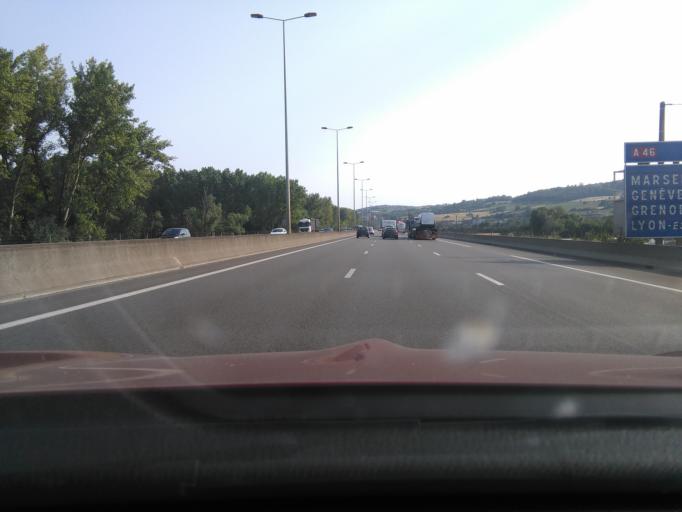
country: FR
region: Rhone-Alpes
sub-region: Departement du Rhone
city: Villefranche-sur-Saone
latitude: 45.9644
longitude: 4.7239
